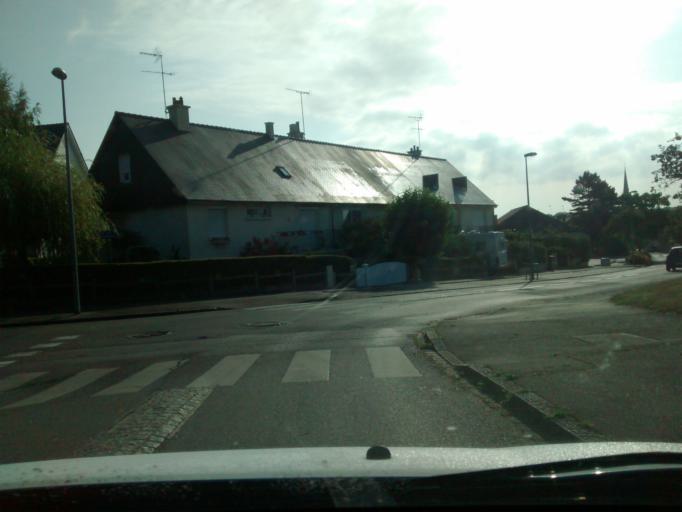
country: FR
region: Brittany
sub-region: Departement d'Ille-et-Vilaine
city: Cesson-Sevigne
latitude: 48.1184
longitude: -1.6117
